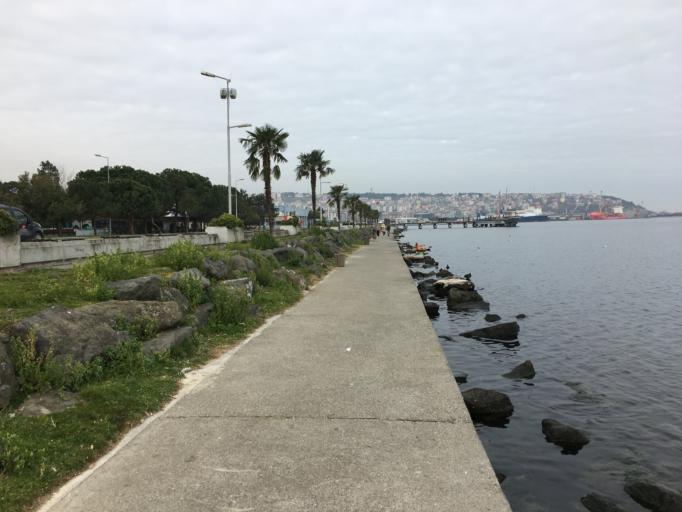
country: TR
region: Samsun
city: Samsun
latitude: 41.2910
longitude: 36.3417
